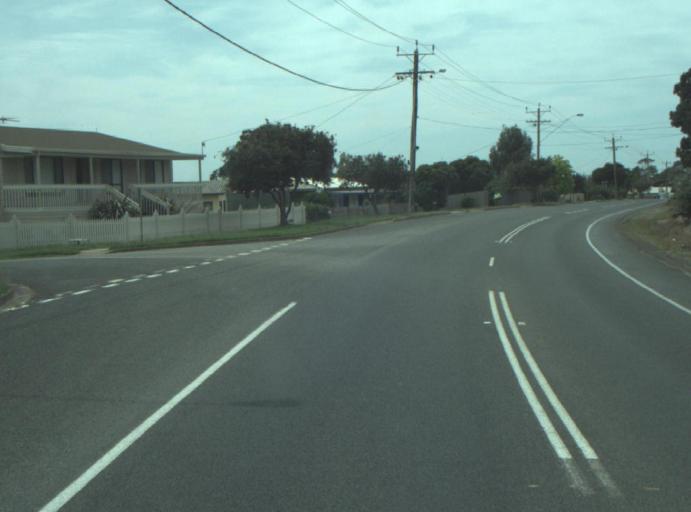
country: AU
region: Victoria
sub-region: Greater Geelong
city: Clifton Springs
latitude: -38.1180
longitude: 144.6396
